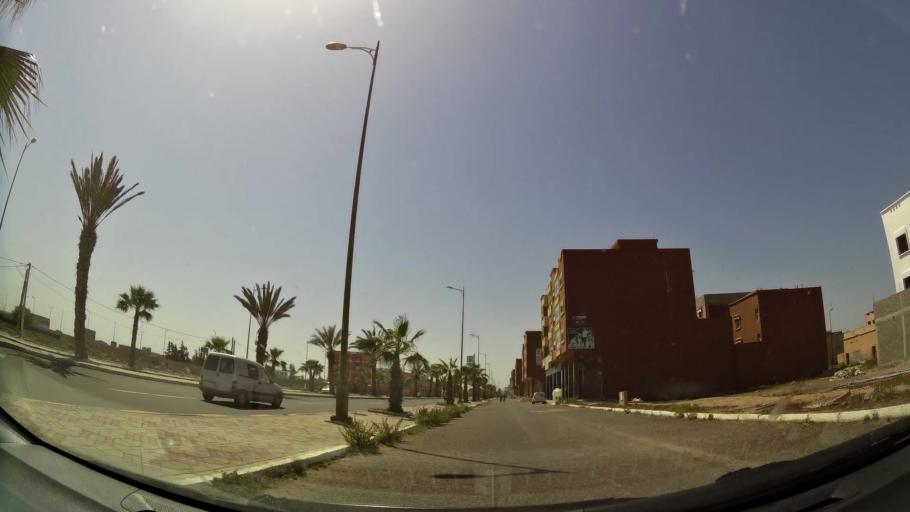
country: MA
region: Souss-Massa-Draa
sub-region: Inezgane-Ait Mellou
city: Inezgane
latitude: 30.3196
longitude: -9.5033
